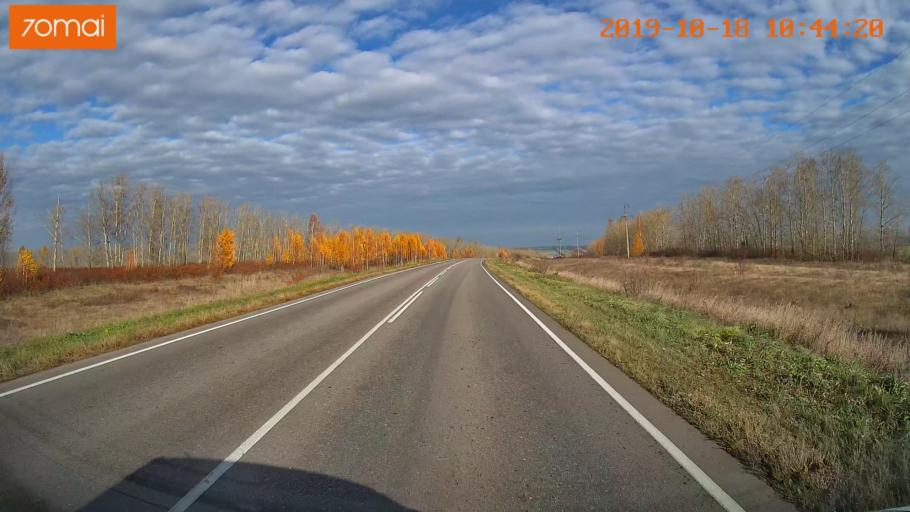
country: RU
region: Tula
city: Yepifan'
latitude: 53.6536
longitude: 38.6821
